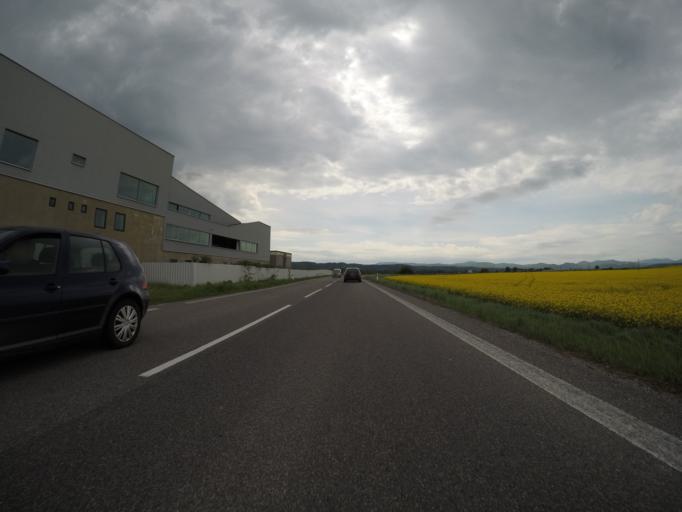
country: SK
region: Banskobystricky
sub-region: Okres Banska Bystrica
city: Zvolen
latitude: 48.6566
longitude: 19.1433
